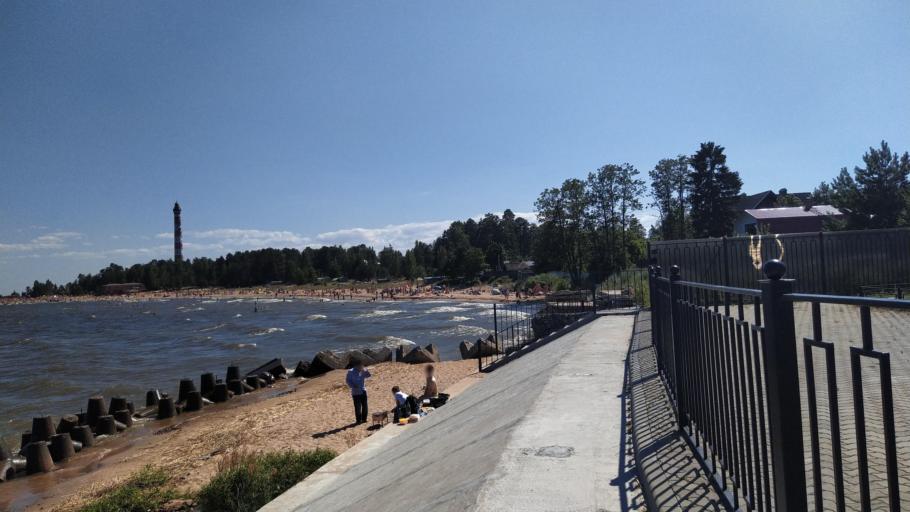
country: RU
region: Leningrad
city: Borisova Griva
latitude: 60.1239
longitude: 31.0768
